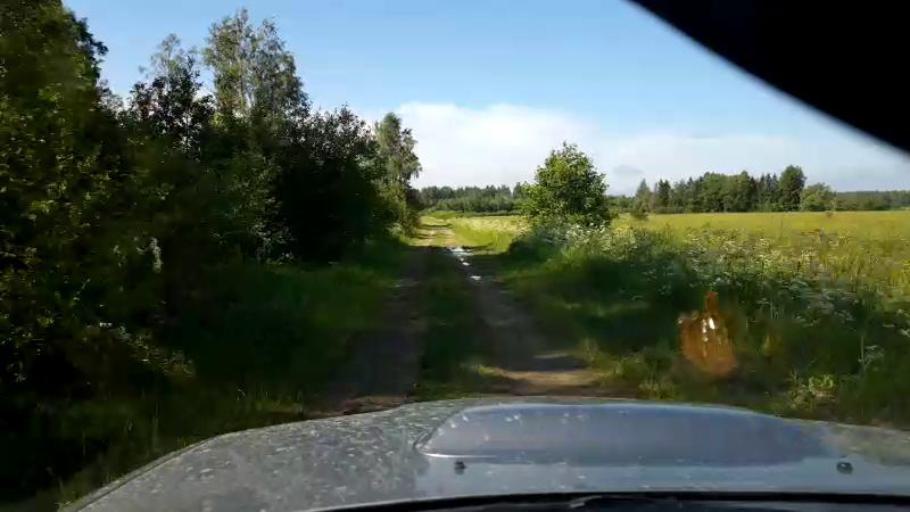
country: EE
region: Paernumaa
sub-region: Sindi linn
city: Sindi
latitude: 58.5067
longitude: 24.6444
